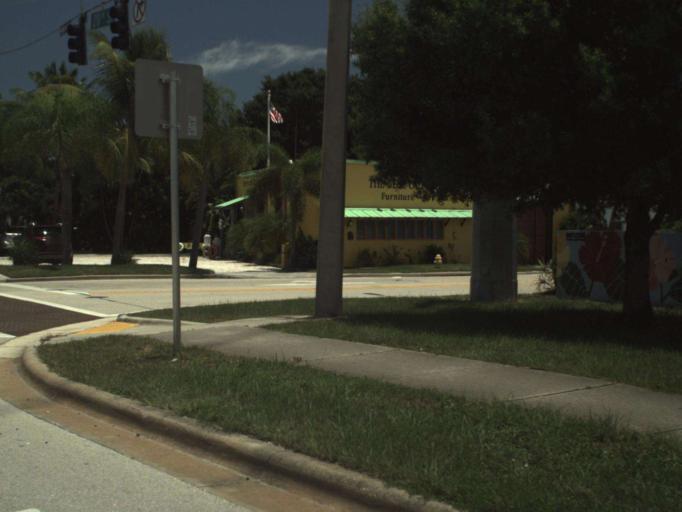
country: US
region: Florida
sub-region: Indian River County
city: Vero Beach
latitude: 27.6378
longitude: -80.3967
